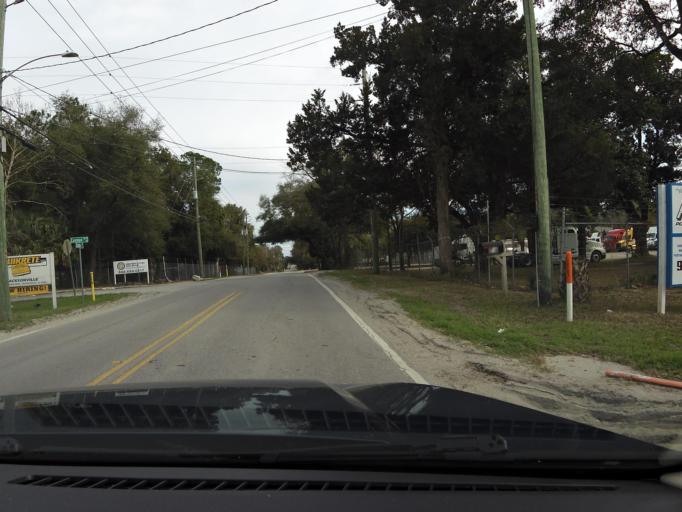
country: US
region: Florida
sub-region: Duval County
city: Jacksonville
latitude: 30.4452
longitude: -81.6206
